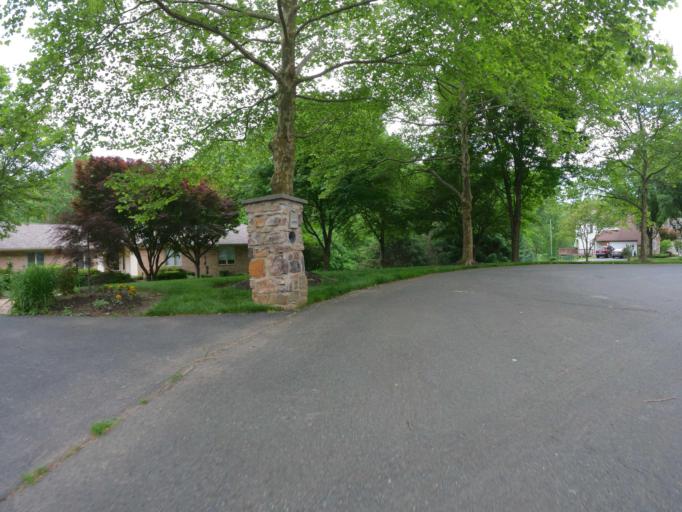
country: US
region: Maryland
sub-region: Howard County
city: Highland
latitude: 39.2240
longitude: -77.0085
